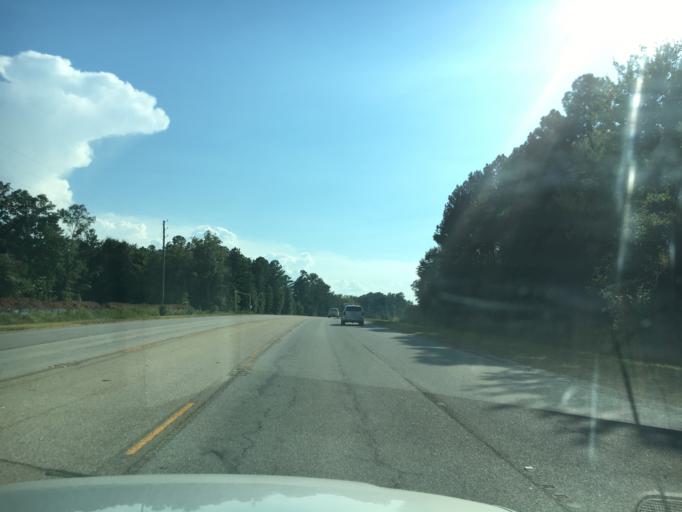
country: US
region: South Carolina
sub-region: Laurens County
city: Clinton
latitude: 34.4255
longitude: -81.9076
